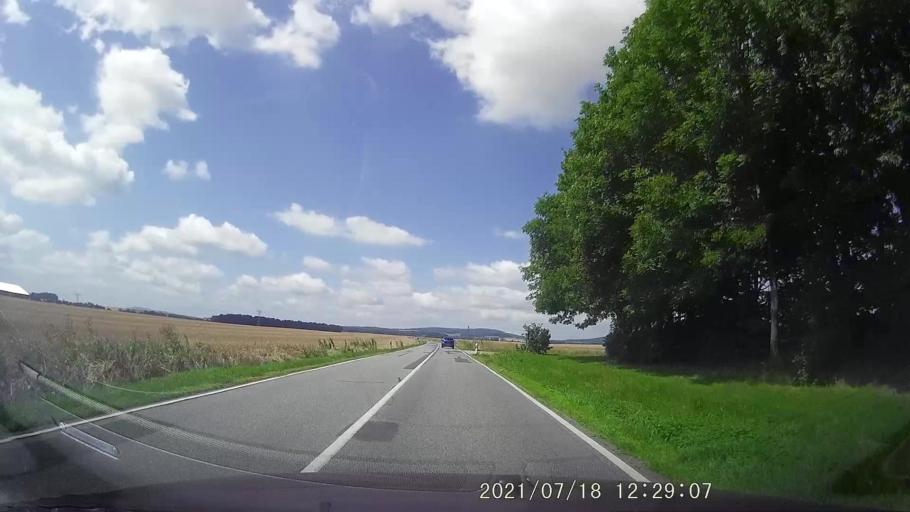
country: DE
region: Saxony
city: Markersdorf
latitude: 51.1674
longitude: 14.9284
